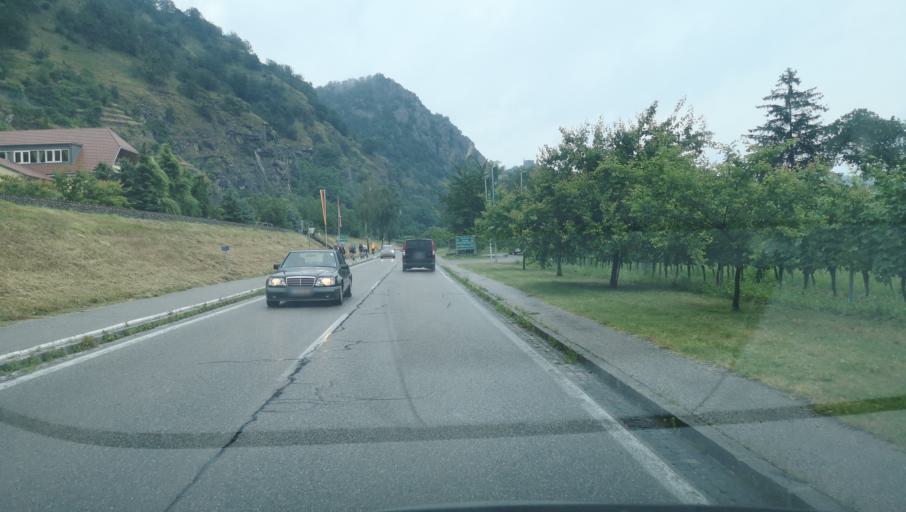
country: AT
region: Lower Austria
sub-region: Politischer Bezirk Krems
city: Durnstein
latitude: 48.4075
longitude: 15.5097
